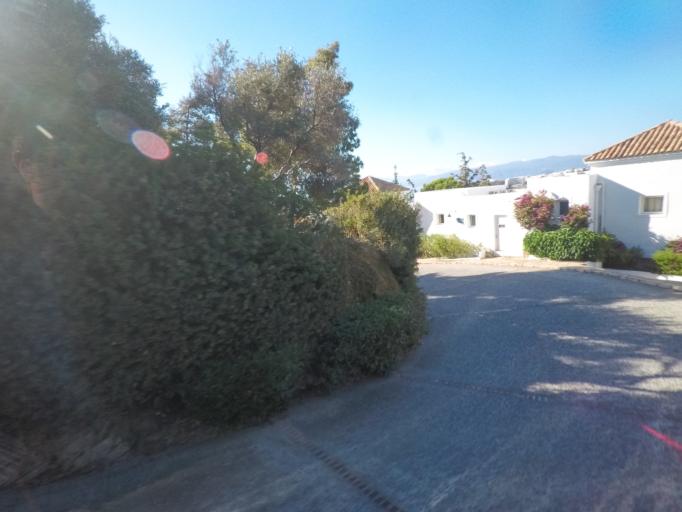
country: GR
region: Crete
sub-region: Nomos Lasithiou
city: Agios Nikolaos
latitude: 35.2189
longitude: 25.7111
